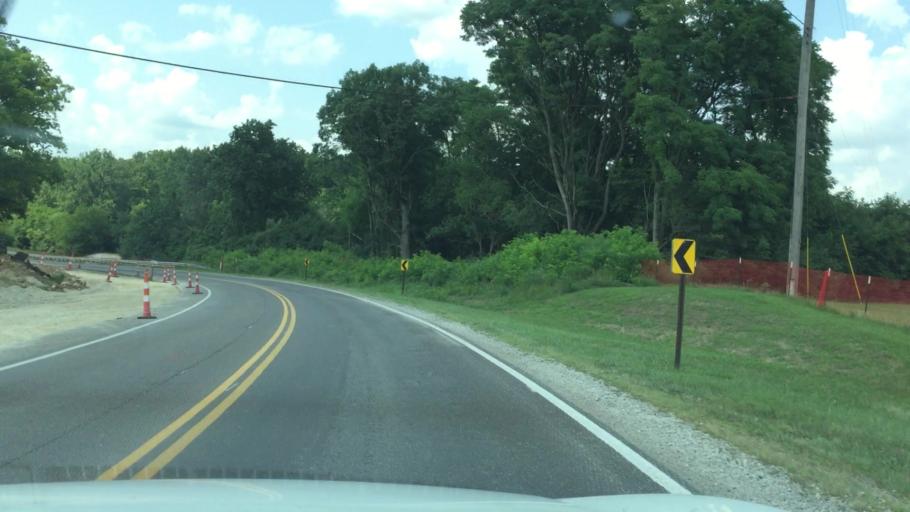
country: US
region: Ohio
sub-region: Clark County
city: Northridge
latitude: 39.9477
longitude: -83.7484
